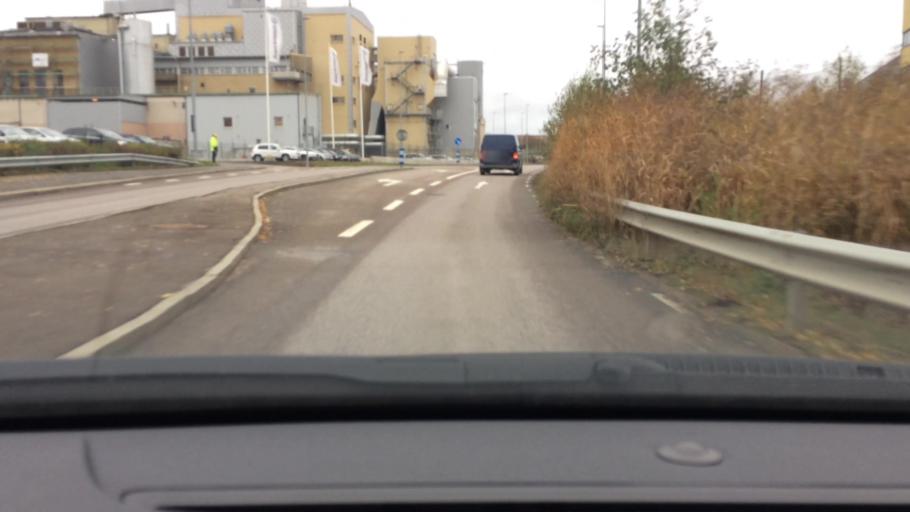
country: SE
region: Vaestra Goetaland
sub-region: Goteborg
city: Eriksbo
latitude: 57.7312
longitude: 12.0330
